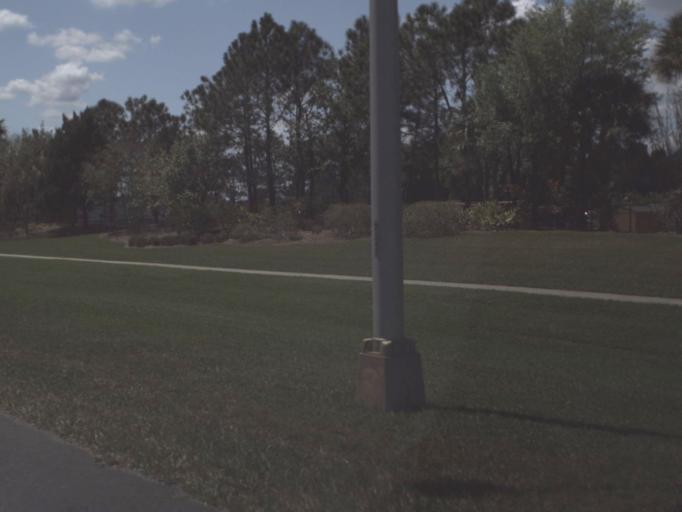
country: US
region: Florida
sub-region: Orange County
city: Williamsburg
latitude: 28.3930
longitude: -81.4253
